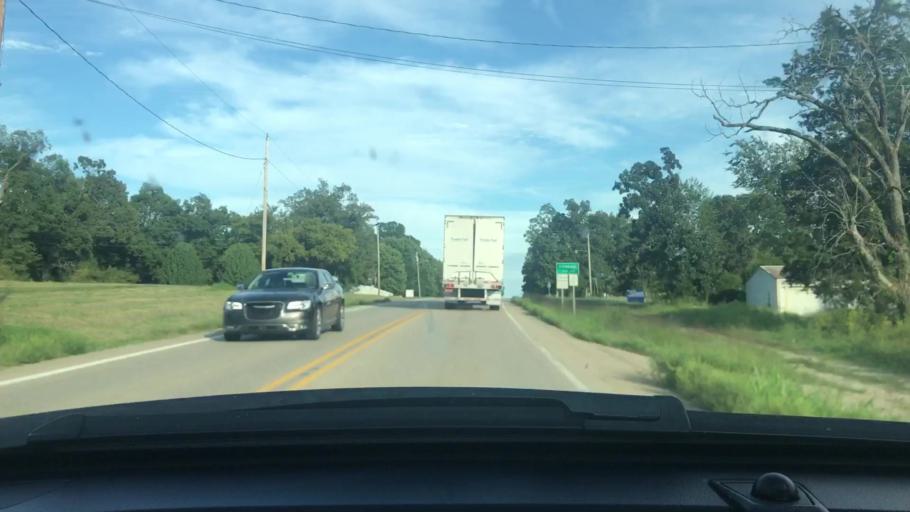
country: US
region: Arkansas
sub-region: Sharp County
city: Cherokee Village
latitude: 36.2392
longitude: -91.2607
